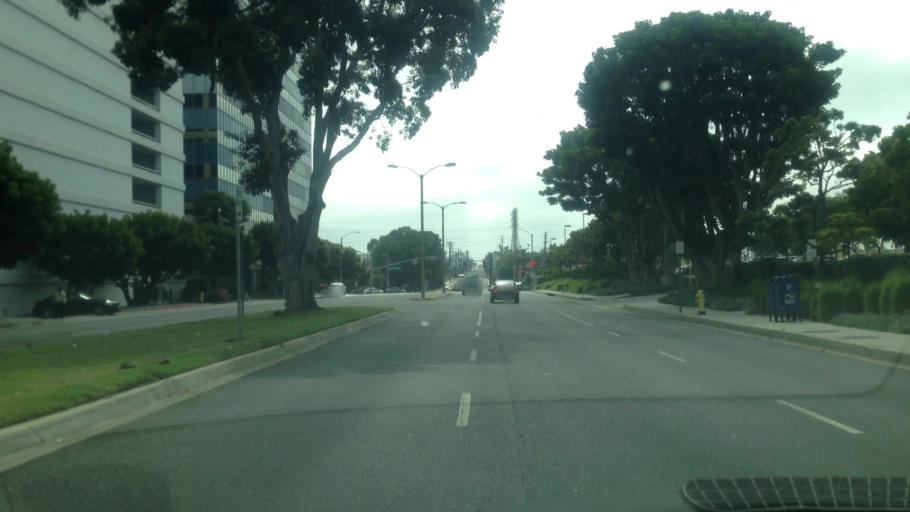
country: US
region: California
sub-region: Los Angeles County
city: El Segundo
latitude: 33.9195
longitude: -118.3937
